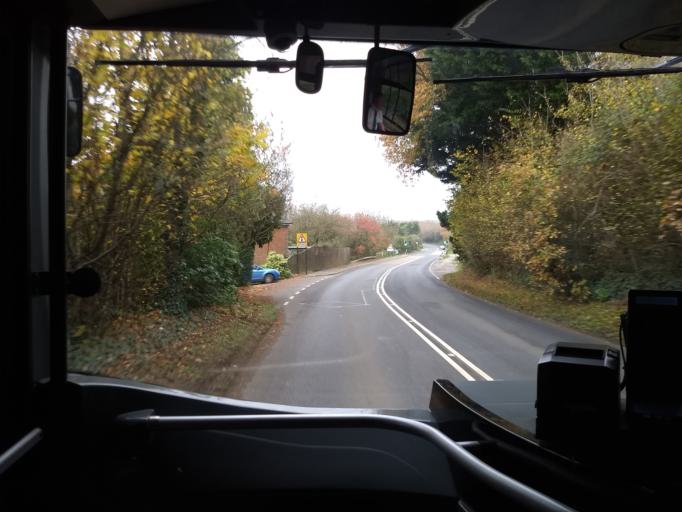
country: GB
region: England
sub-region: Isle of Wight
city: Newchurch
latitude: 50.6654
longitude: -1.2324
